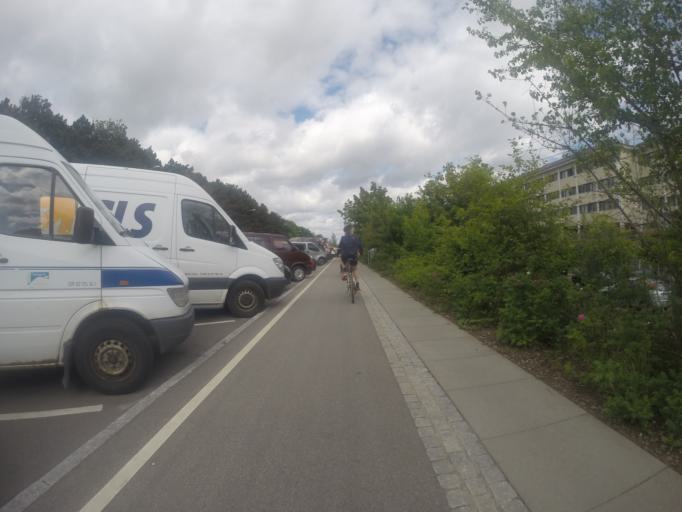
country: DK
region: Capital Region
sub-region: Hoje-Taastrup Kommune
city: Taastrup
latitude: 55.6550
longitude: 12.2889
